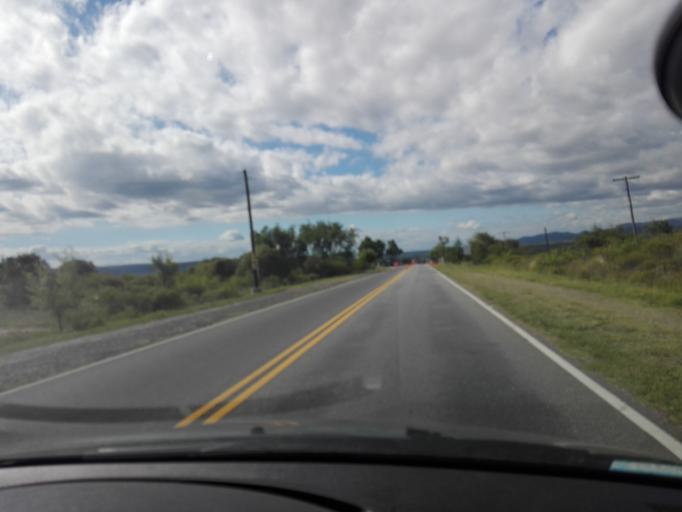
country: AR
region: Cordoba
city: Mina Clavero
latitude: -31.7526
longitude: -64.9770
